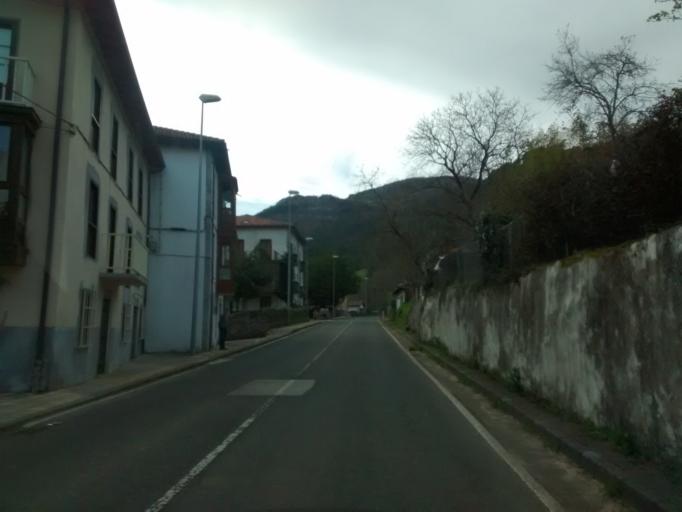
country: ES
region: Cantabria
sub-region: Provincia de Cantabria
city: Arredondo
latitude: 43.2751
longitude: -3.6030
